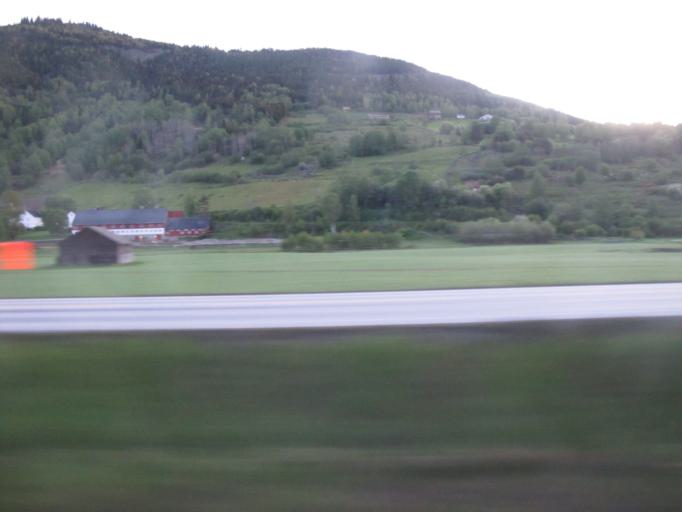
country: NO
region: Oppland
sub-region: Sor-Fron
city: Hundorp
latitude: 61.5478
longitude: 10.0351
